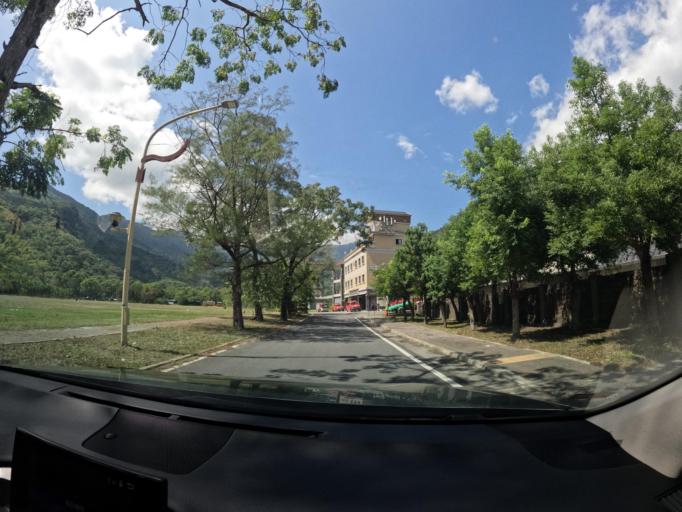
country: TW
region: Taiwan
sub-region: Hualien
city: Hualian
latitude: 23.7190
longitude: 121.4052
